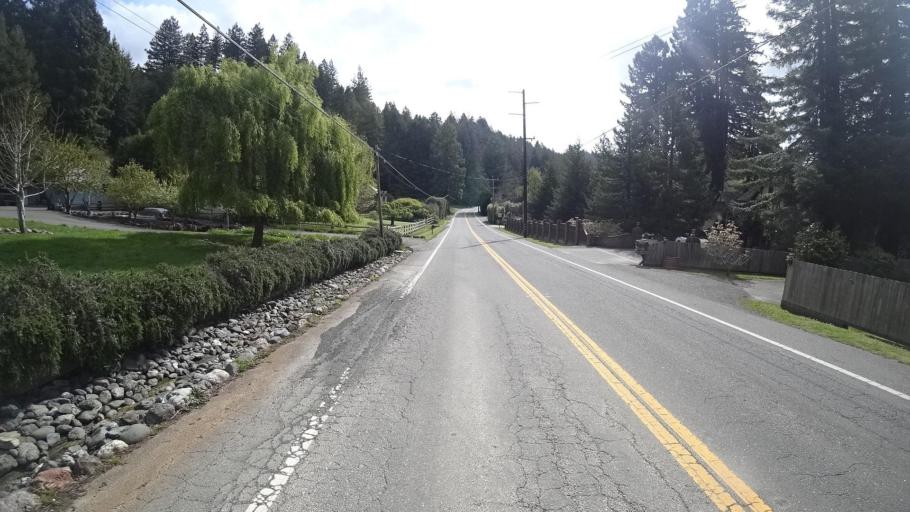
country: US
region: California
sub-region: Humboldt County
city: Myrtletown
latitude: 40.7601
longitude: -124.0564
